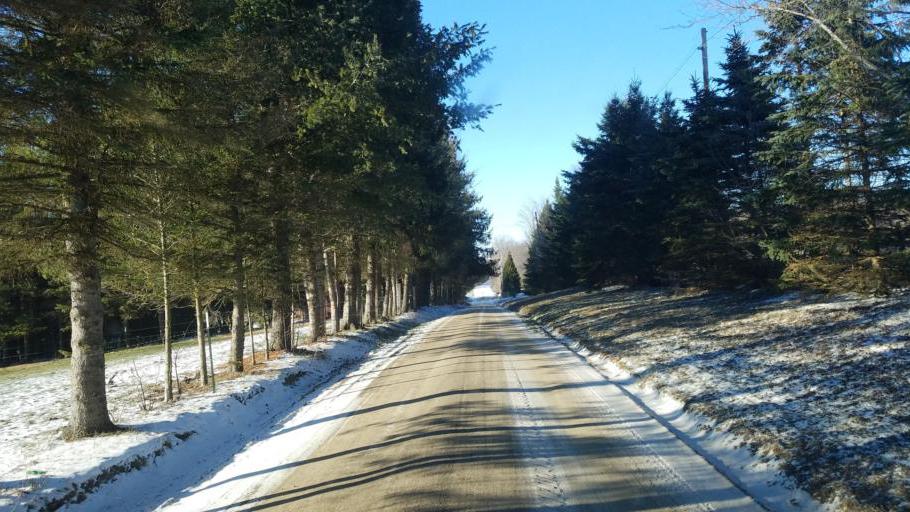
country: US
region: Pennsylvania
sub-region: Potter County
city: Galeton
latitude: 41.9039
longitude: -77.7464
